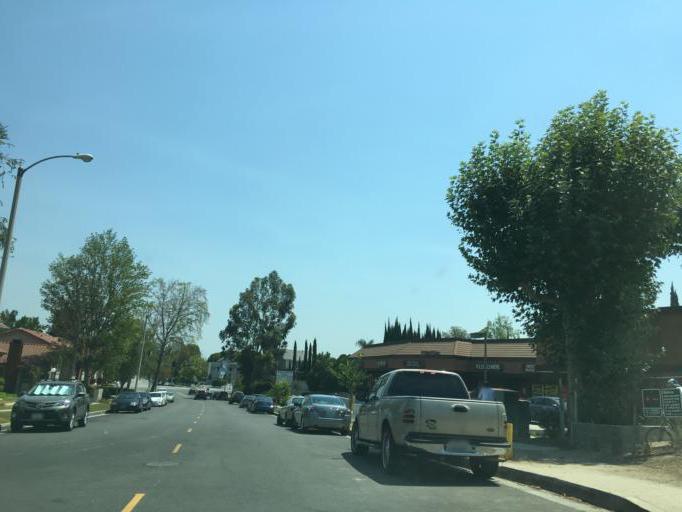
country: US
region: California
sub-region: Los Angeles County
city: West Hills
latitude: 34.1954
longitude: -118.6586
